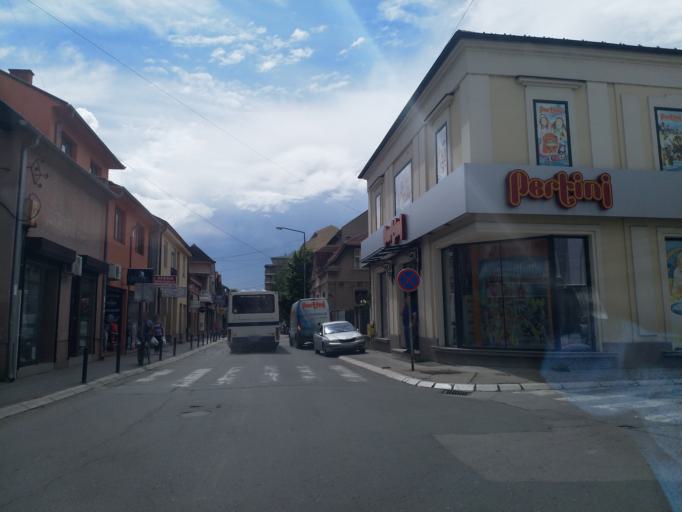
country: RS
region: Central Serbia
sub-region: Pomoravski Okrug
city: Paracin
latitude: 43.8597
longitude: 21.4134
